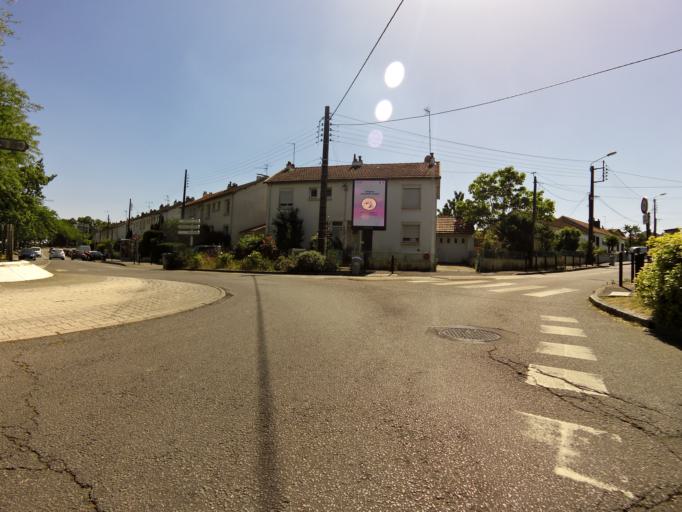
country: FR
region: Pays de la Loire
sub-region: Departement de la Loire-Atlantique
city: Saint-Herblain
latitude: 47.2246
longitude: -1.6033
